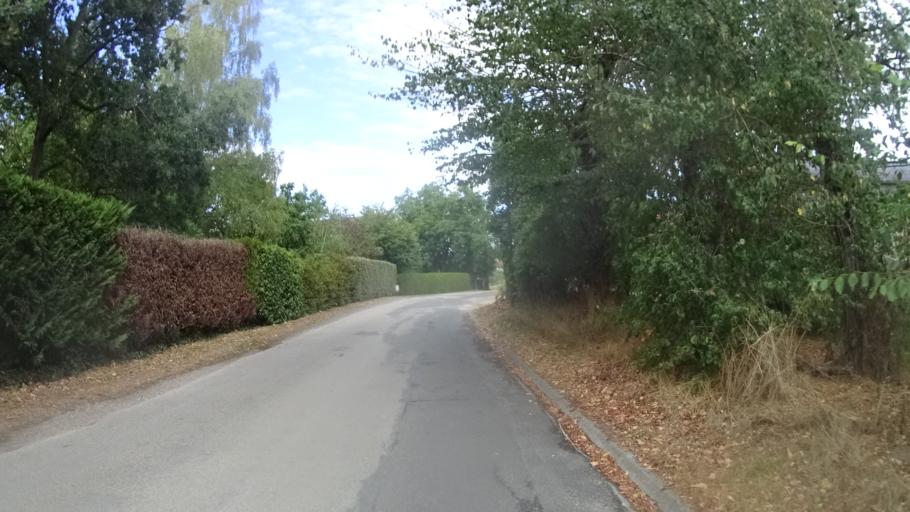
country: FR
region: Centre
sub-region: Departement du Loiret
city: Malesherbes
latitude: 48.2581
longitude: 2.4298
